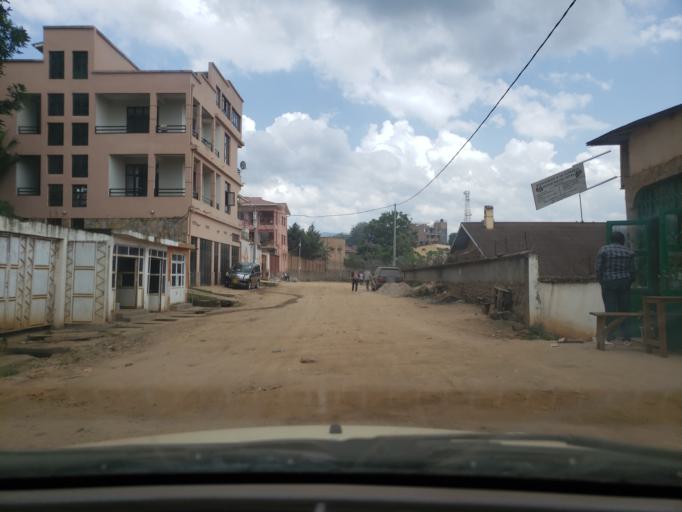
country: RW
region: Western Province
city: Cyangugu
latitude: -2.4989
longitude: 28.8821
